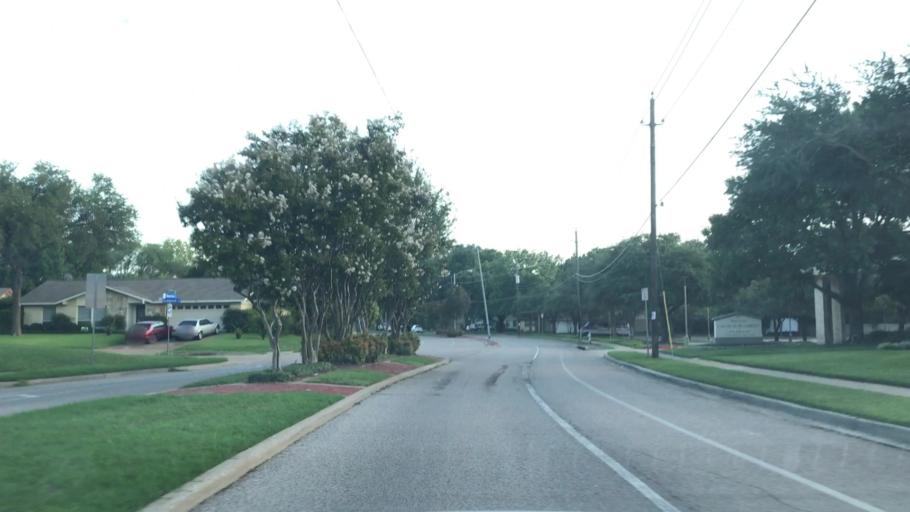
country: US
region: Texas
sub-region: Dallas County
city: Richardson
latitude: 32.9687
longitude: -96.7548
